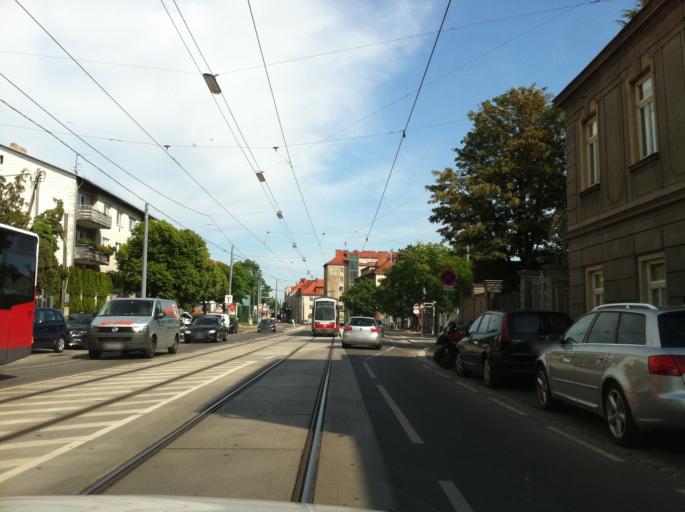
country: AT
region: Lower Austria
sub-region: Politischer Bezirk Modling
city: Perchtoldsdorf
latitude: 48.2004
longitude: 16.2662
